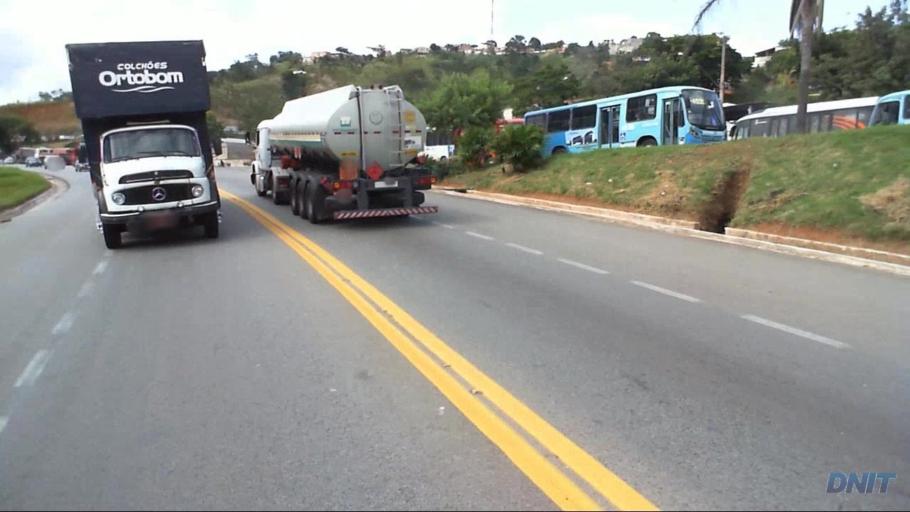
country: BR
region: Minas Gerais
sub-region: Santa Luzia
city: Santa Luzia
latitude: -19.8328
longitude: -43.8464
